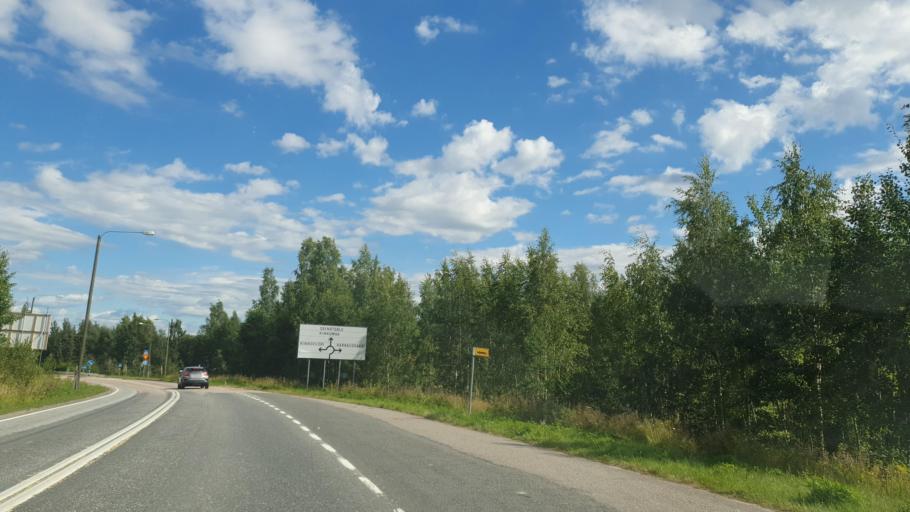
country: FI
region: Central Finland
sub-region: Jyvaeskylae
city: Saeynaetsalo
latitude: 62.1374
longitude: 25.7322
